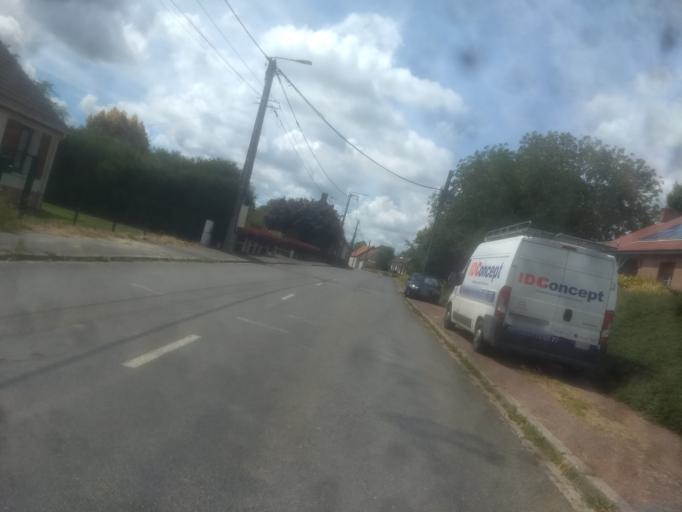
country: FR
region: Nord-Pas-de-Calais
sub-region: Departement du Pas-de-Calais
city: Mont-Saint-Eloi
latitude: 50.3466
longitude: 2.6601
